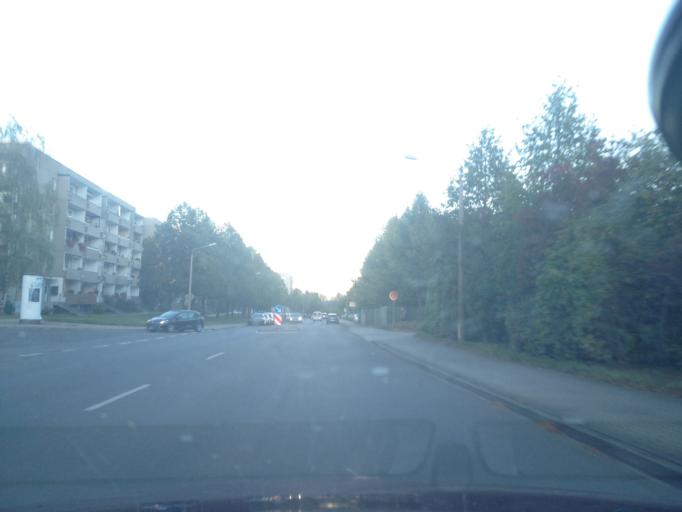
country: DE
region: Saxony
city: Goerlitz
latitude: 51.1698
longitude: 14.9813
